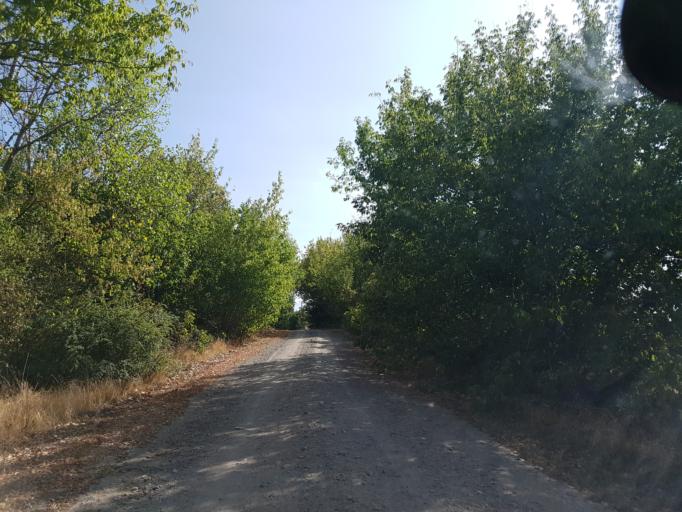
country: DE
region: Brandenburg
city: Treuenbrietzen
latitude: 51.9977
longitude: 12.8570
